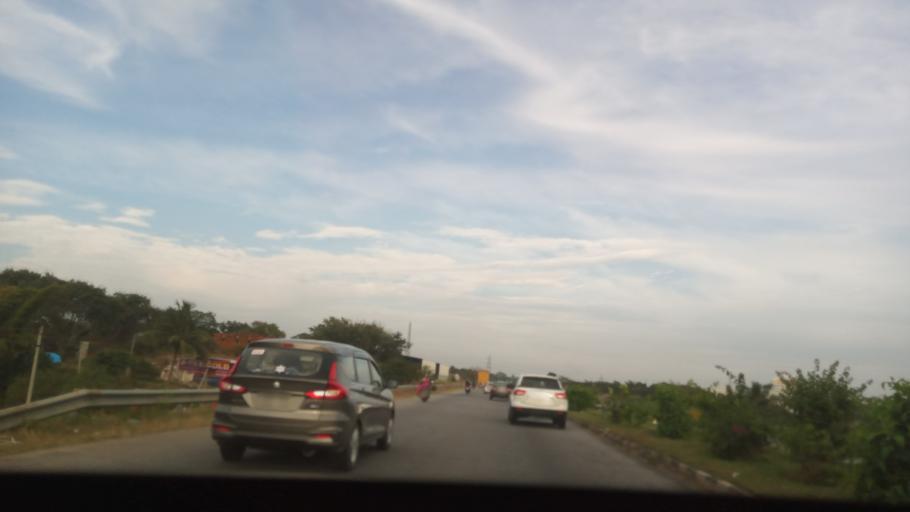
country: IN
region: Karnataka
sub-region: Ramanagara
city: Magadi
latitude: 13.0728
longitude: 77.1902
